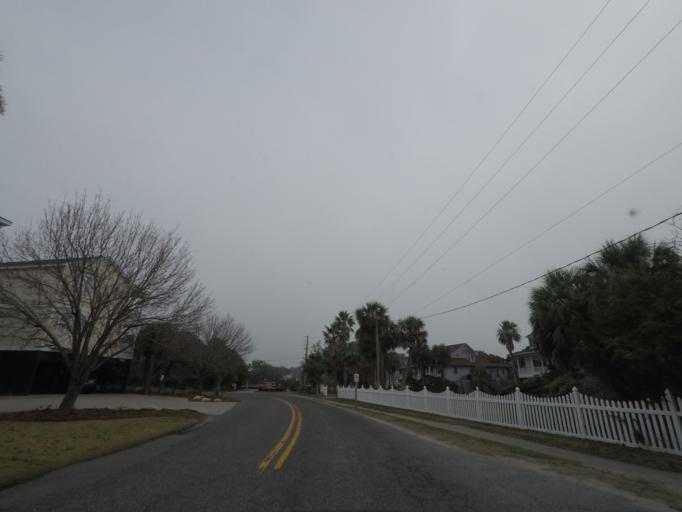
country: US
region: South Carolina
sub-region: Charleston County
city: Seabrook Island
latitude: 32.4924
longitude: -80.3402
